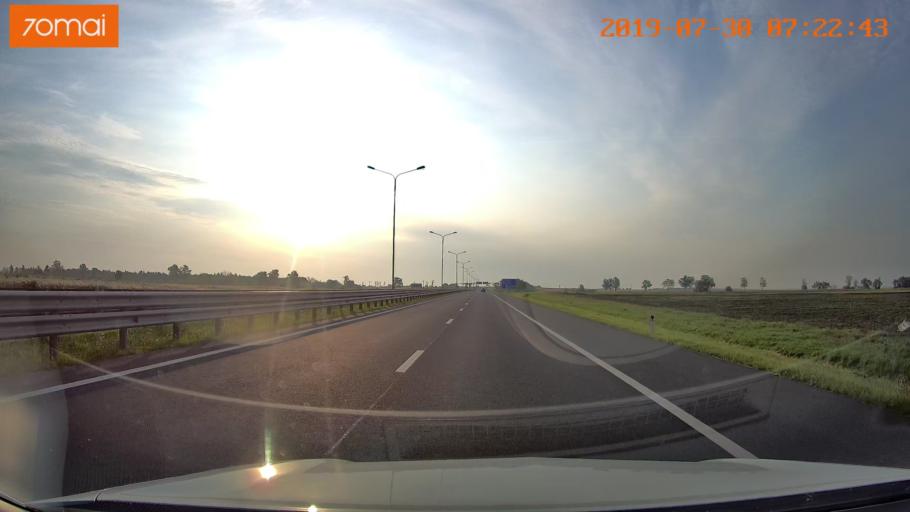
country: RU
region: Kaliningrad
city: Bol'shoe Isakovo
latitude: 54.6922
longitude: 20.7637
